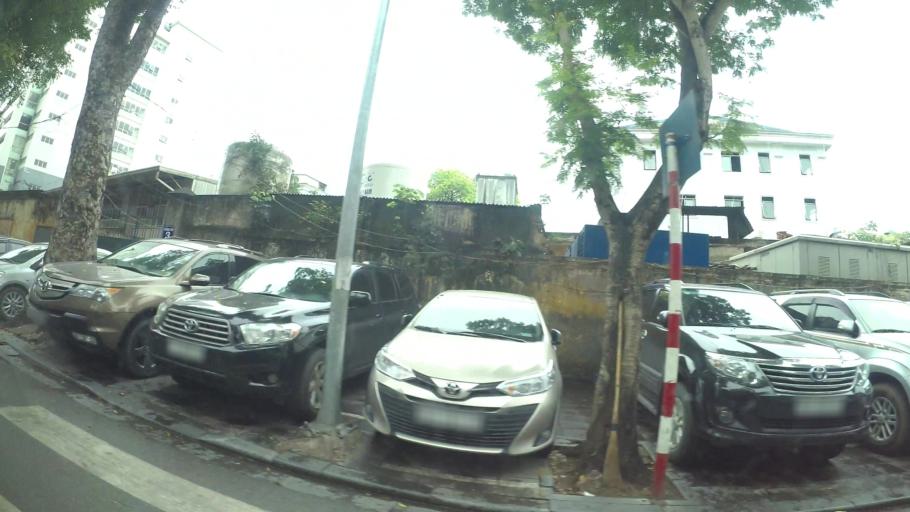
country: VN
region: Ha Noi
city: Hoan Kiem
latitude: 21.0293
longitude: 105.8476
